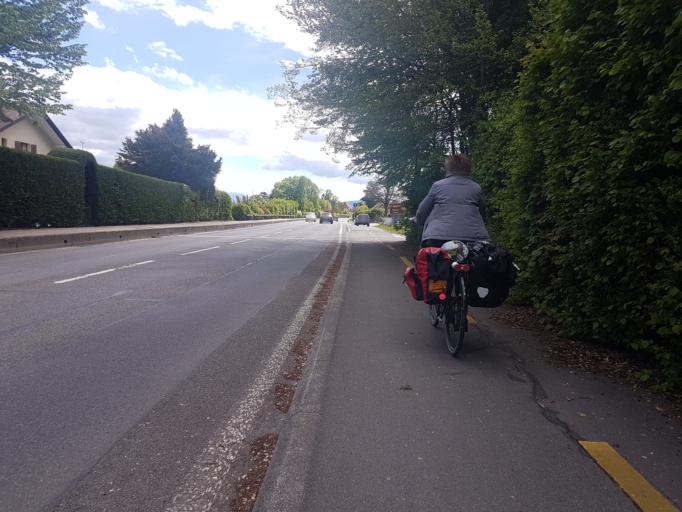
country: CH
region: Vaud
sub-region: Nyon District
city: Founex
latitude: 46.3352
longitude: 6.2023
